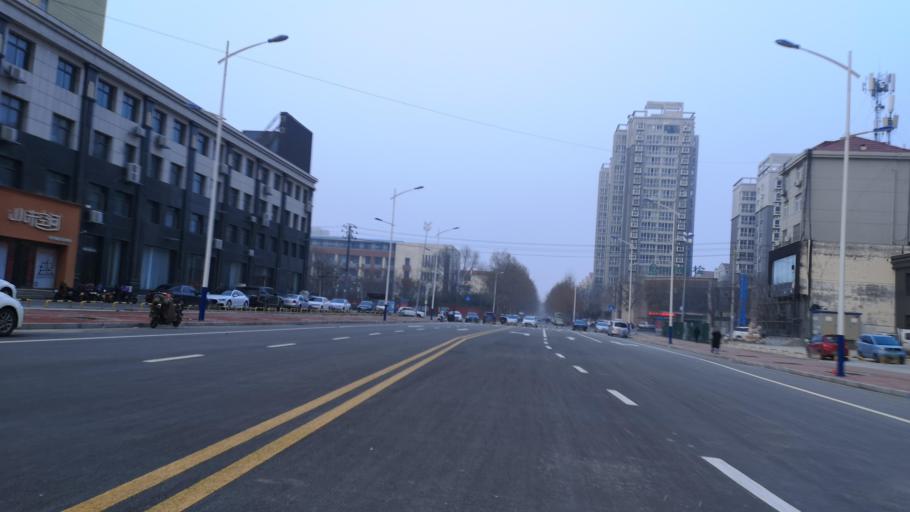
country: CN
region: Henan Sheng
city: Zhongyuanlu
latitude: 35.7522
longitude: 115.0604
